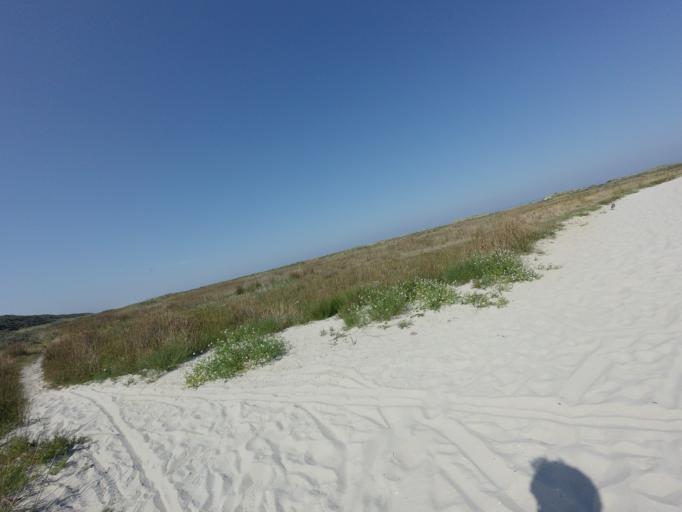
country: NL
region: Friesland
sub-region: Gemeente Schiermonnikoog
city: Schiermonnikoog
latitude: 53.4998
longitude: 6.2450
